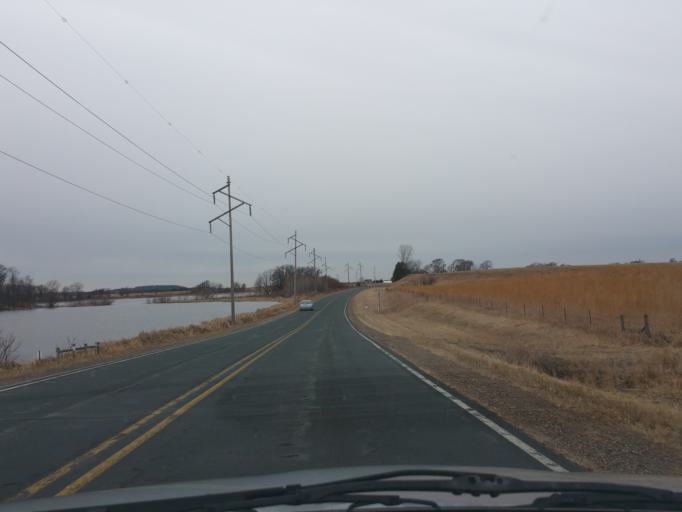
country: US
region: Wisconsin
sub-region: Saint Croix County
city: Roberts
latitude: 45.0358
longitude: -92.5848
